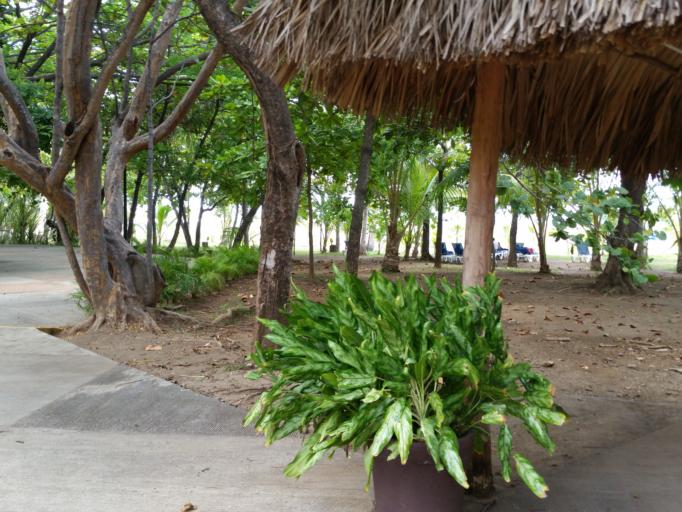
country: NI
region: Managua
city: Masachapa
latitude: 11.8078
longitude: -86.5212
